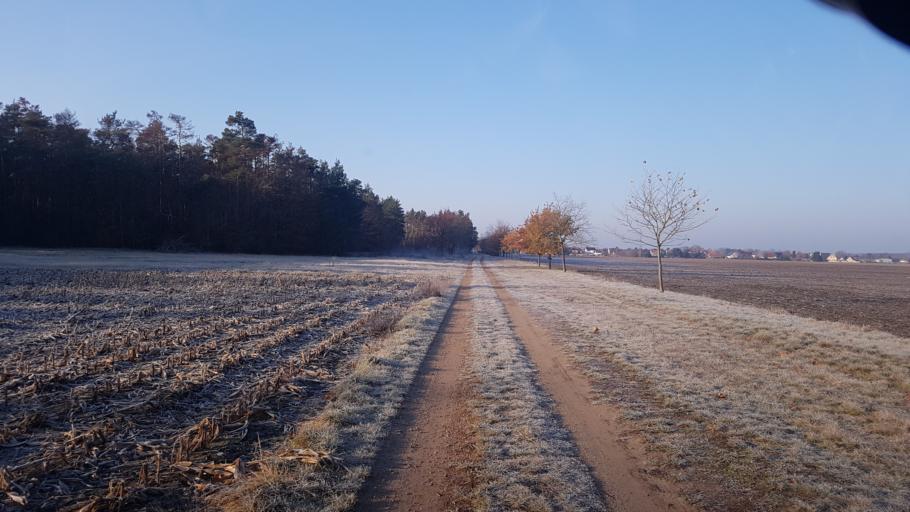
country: DE
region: Brandenburg
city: Tettau
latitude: 51.4297
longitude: 13.7458
